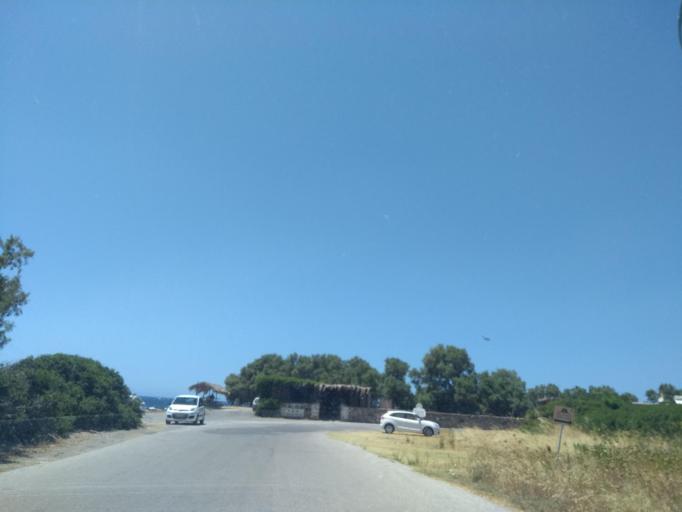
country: GR
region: Crete
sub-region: Nomos Chanias
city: Vryses
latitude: 35.3595
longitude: 23.5318
